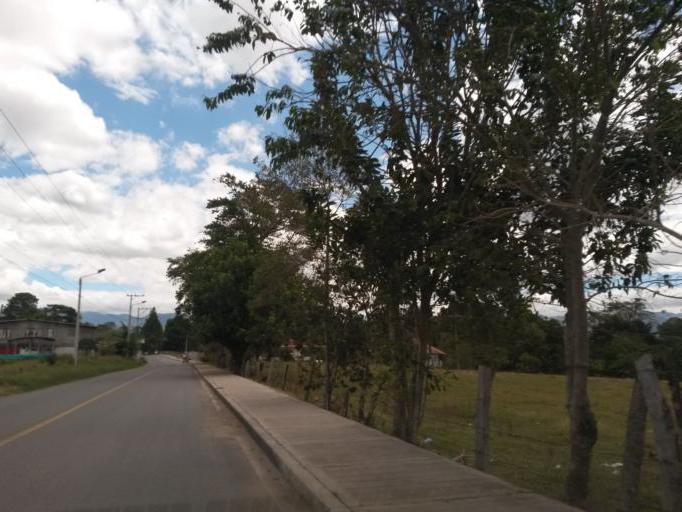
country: CO
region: Cauca
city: Popayan
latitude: 2.4886
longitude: -76.5891
